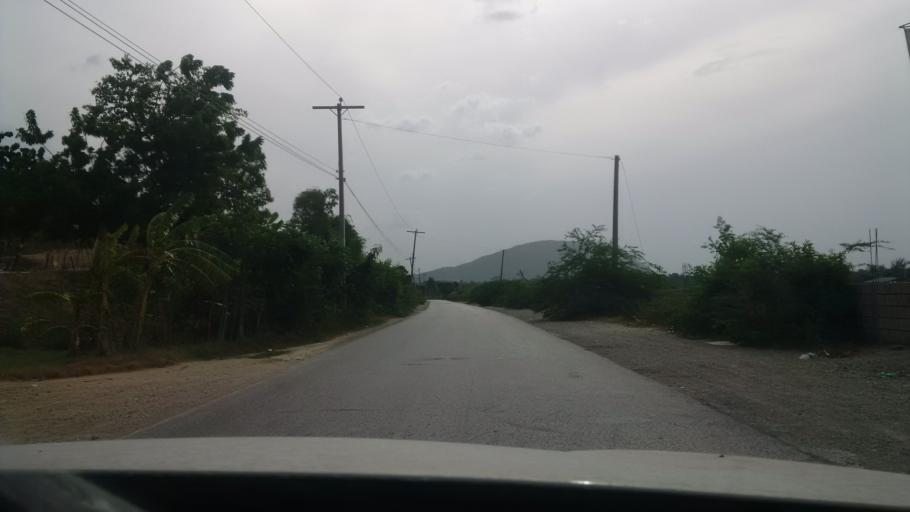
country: HT
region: Ouest
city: Grangwav
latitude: 18.4253
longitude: -72.7498
